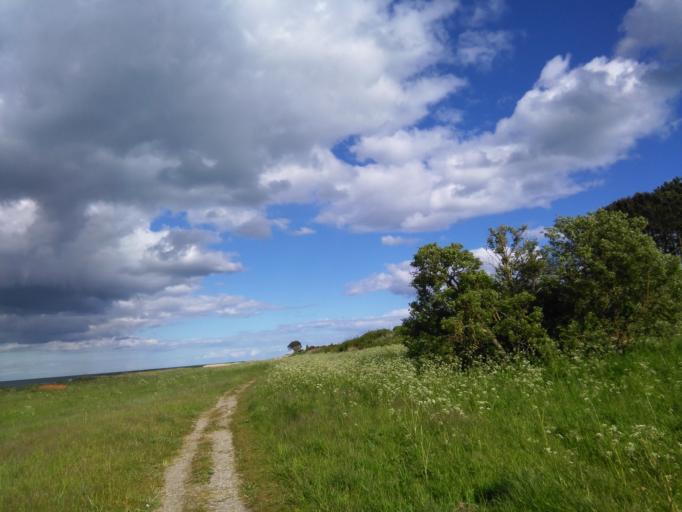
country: DK
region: Central Jutland
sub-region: Arhus Kommune
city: Beder
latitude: 56.0229
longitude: 10.2689
